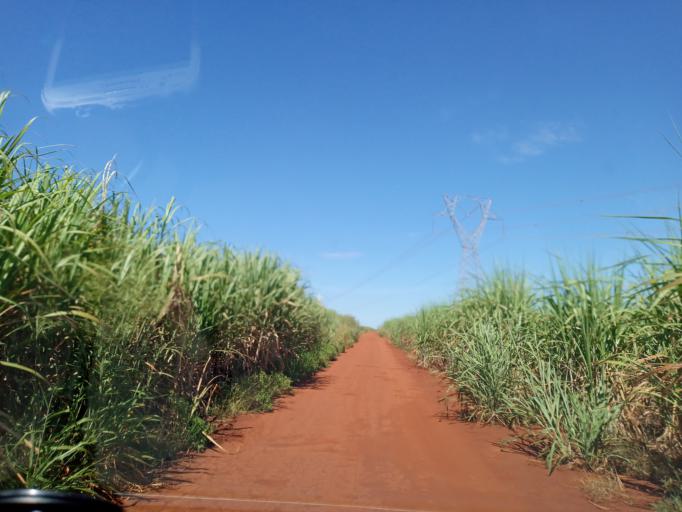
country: BR
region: Goias
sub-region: Itumbiara
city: Itumbiara
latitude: -18.4532
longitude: -49.1454
